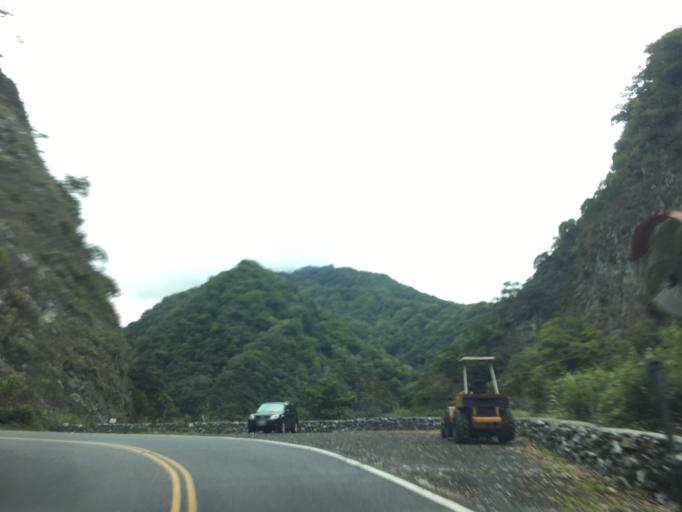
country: TW
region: Taiwan
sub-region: Hualien
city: Hualian
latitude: 24.2145
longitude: 121.4836
